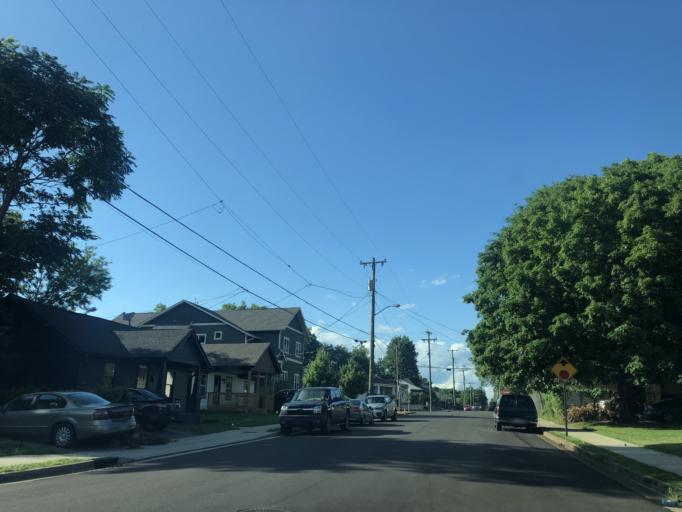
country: US
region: Tennessee
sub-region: Davidson County
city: Nashville
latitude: 36.1834
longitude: -86.7636
